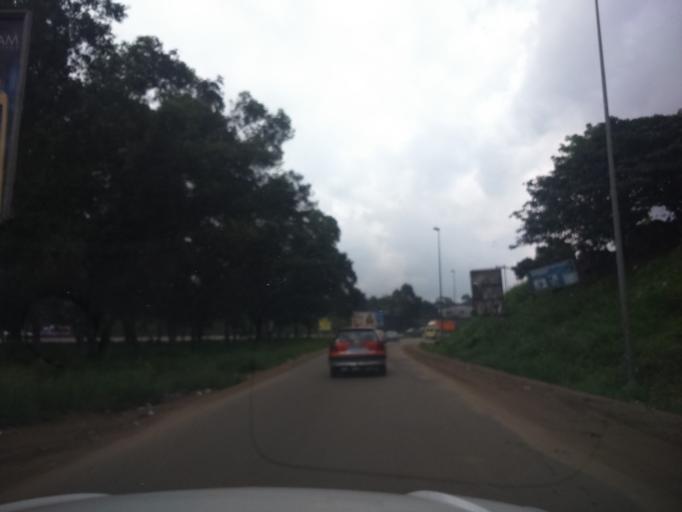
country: CI
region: Lagunes
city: Abidjan
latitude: 5.3586
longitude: -4.0656
